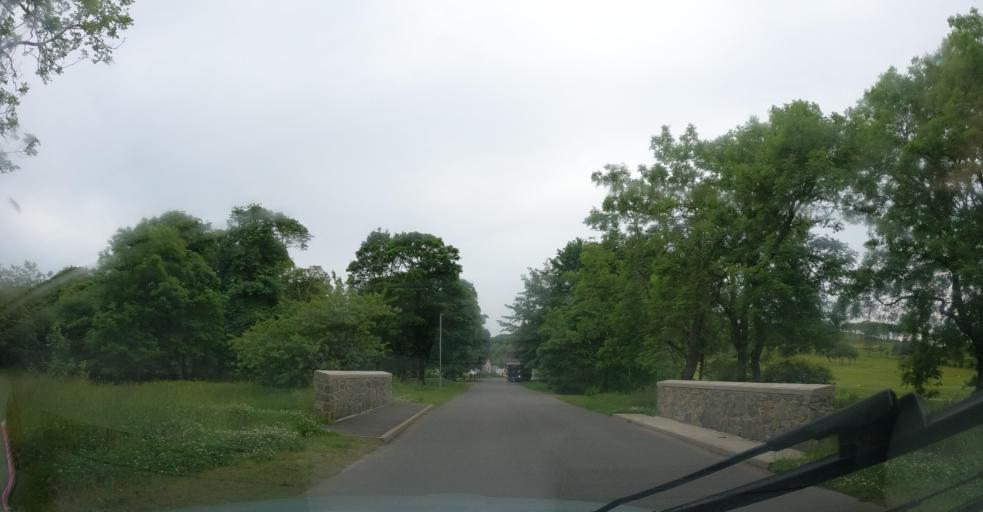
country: GB
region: Scotland
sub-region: Eilean Siar
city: Isle of Lewis
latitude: 58.2165
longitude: -6.3872
